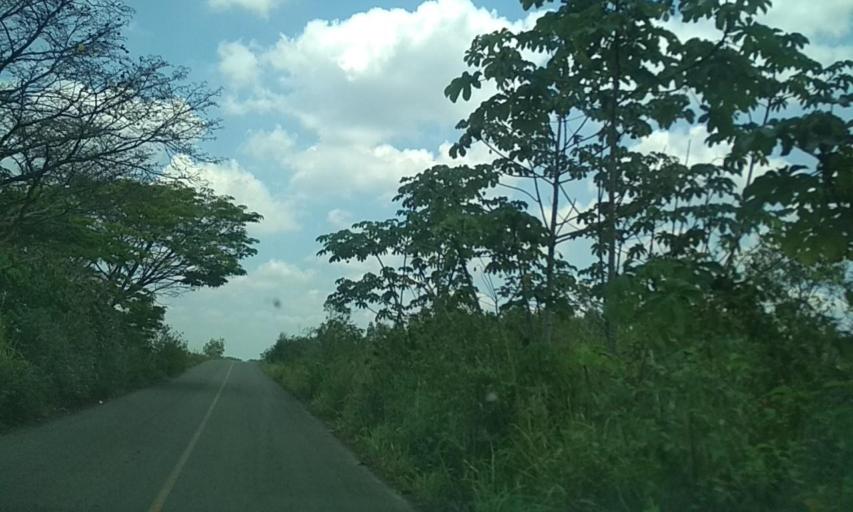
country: MX
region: Tabasco
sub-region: Huimanguillo
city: Francisco Rueda
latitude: 17.7919
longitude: -93.8440
